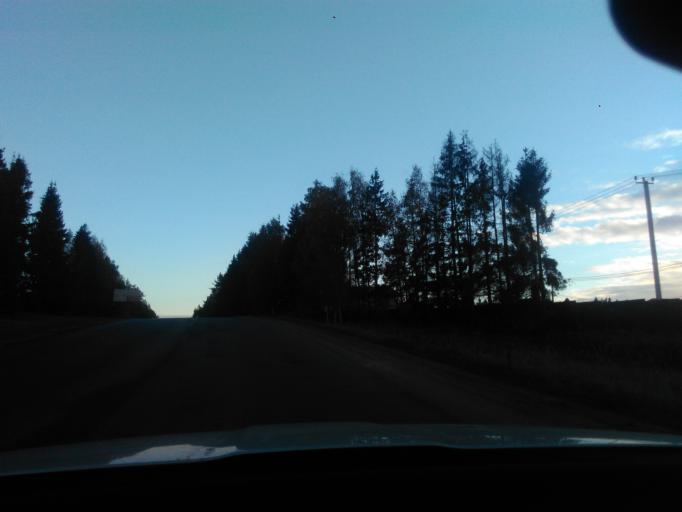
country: RU
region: Moskovskaya
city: Solnechnogorsk
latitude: 56.1087
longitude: 36.9123
